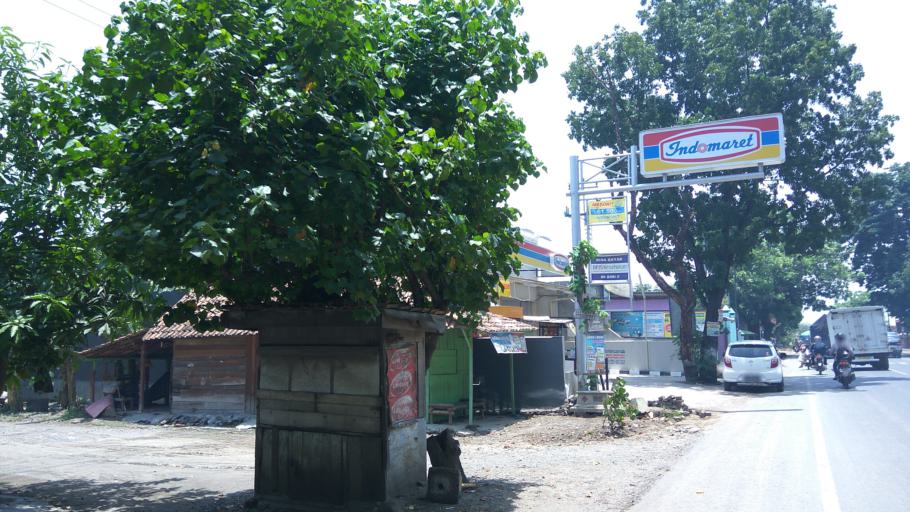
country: ID
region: Central Java
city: Mranggen
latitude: -7.0308
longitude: 110.5371
